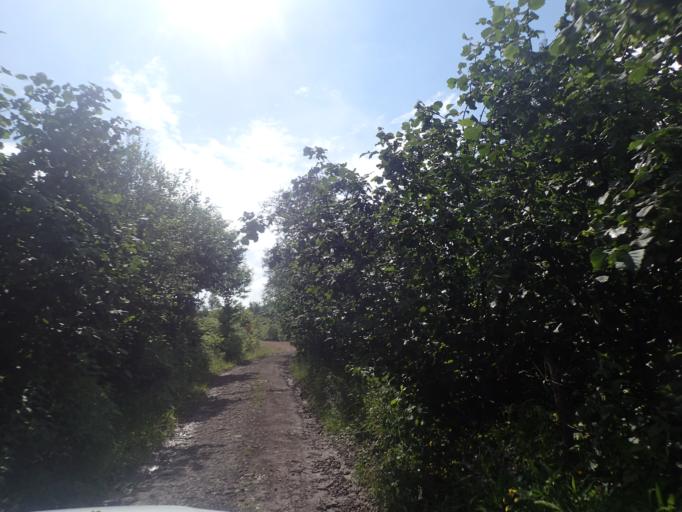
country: TR
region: Ordu
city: Akkus
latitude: 40.8954
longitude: 36.9860
